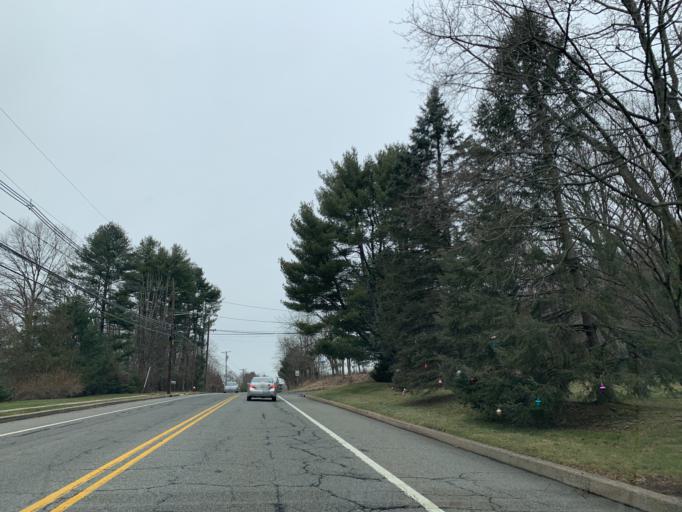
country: US
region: New Jersey
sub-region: Somerset County
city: Martinsville
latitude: 40.6186
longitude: -74.5857
